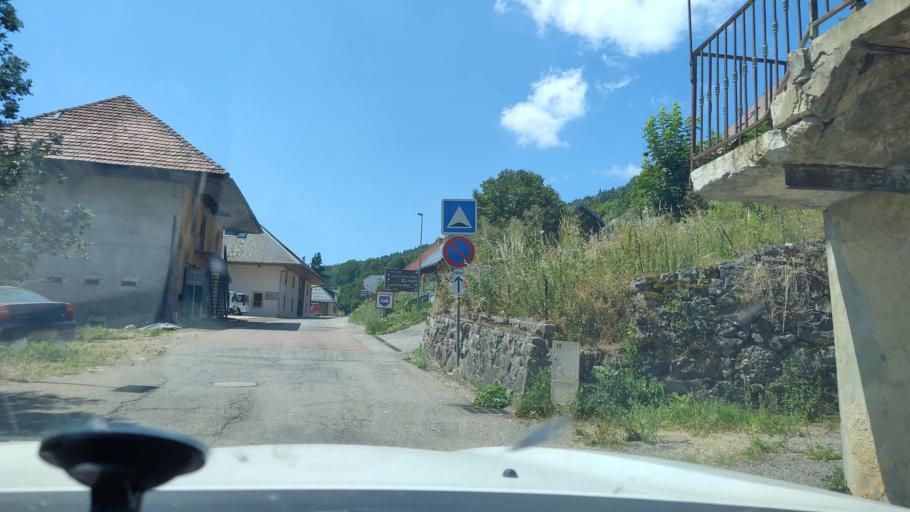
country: FR
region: Rhone-Alpes
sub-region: Departement de la Haute-Savoie
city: Cusy
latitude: 45.6684
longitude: 6.0370
